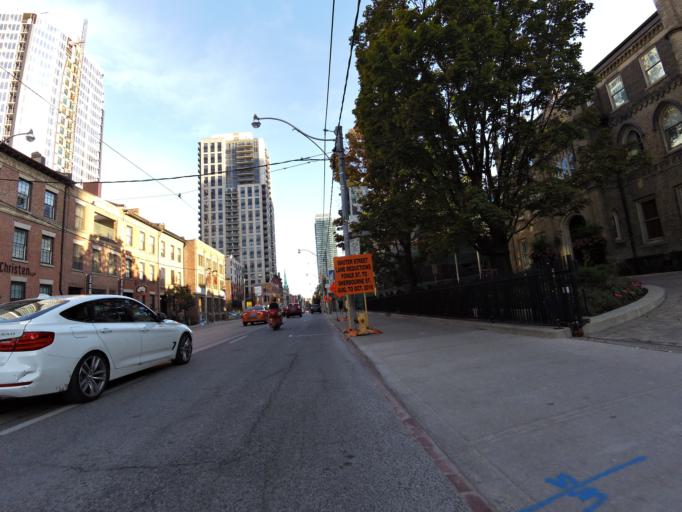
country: CA
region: Ontario
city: Toronto
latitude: 43.6557
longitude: -79.3769
